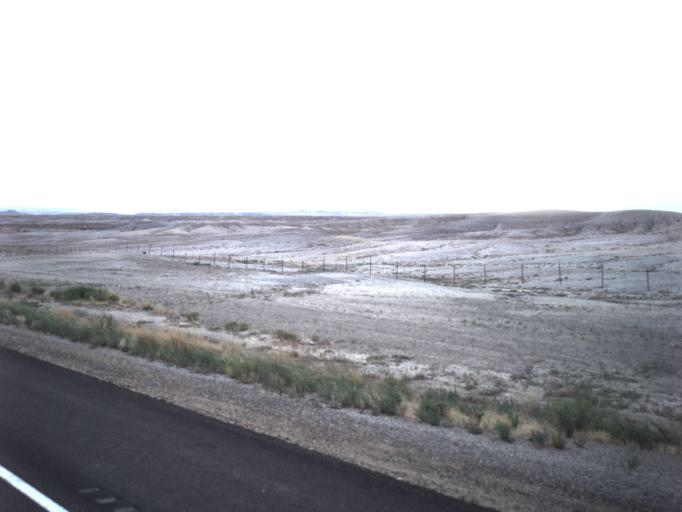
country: US
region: Utah
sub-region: Carbon County
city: East Carbon City
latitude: 38.9873
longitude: -110.2426
